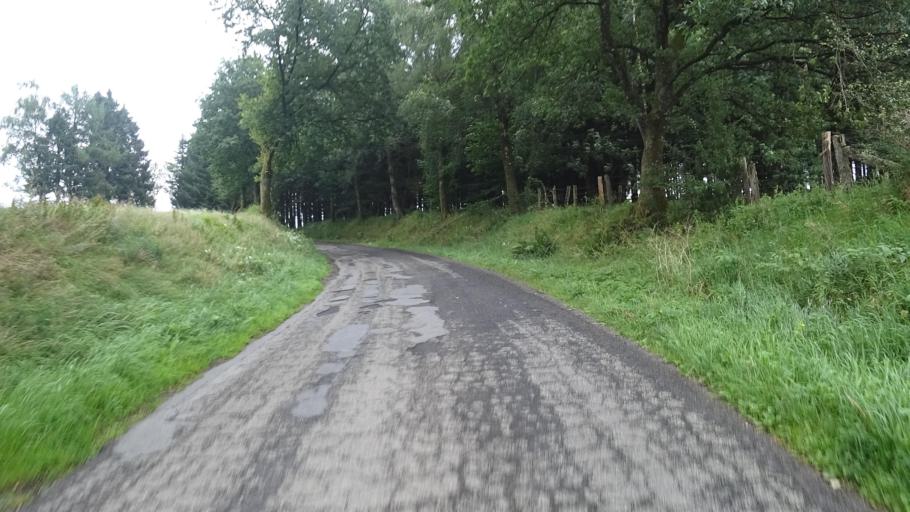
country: BE
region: Wallonia
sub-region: Province du Luxembourg
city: Chiny
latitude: 49.8086
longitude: 5.3361
